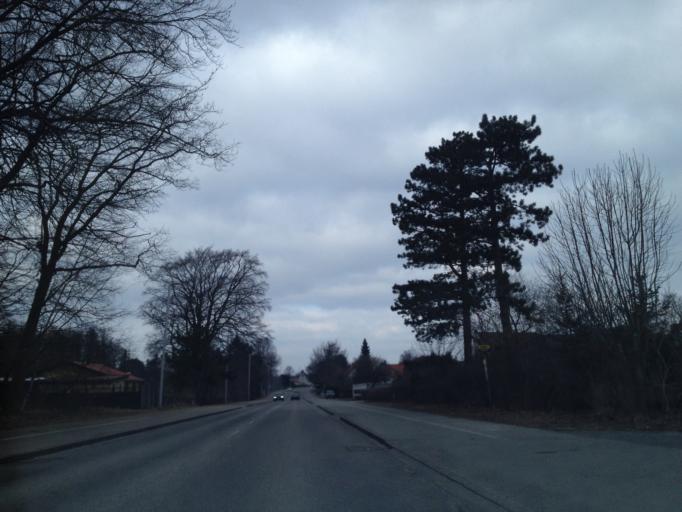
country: DK
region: Capital Region
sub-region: Fredensborg Kommune
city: Humlebaek
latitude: 55.9771
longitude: 12.5442
